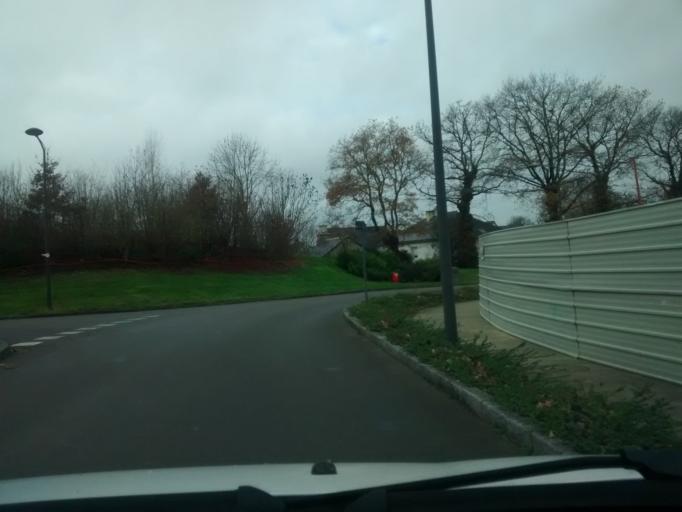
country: FR
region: Brittany
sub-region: Departement d'Ille-et-Vilaine
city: Fouillard
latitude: 48.1605
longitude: -1.5807
